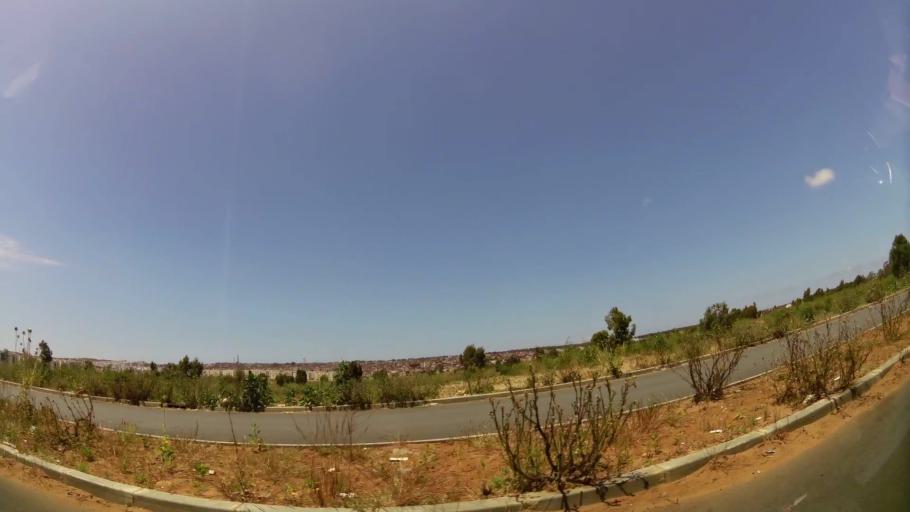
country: MA
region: Gharb-Chrarda-Beni Hssen
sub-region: Kenitra Province
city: Kenitra
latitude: 34.2559
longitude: -6.6302
